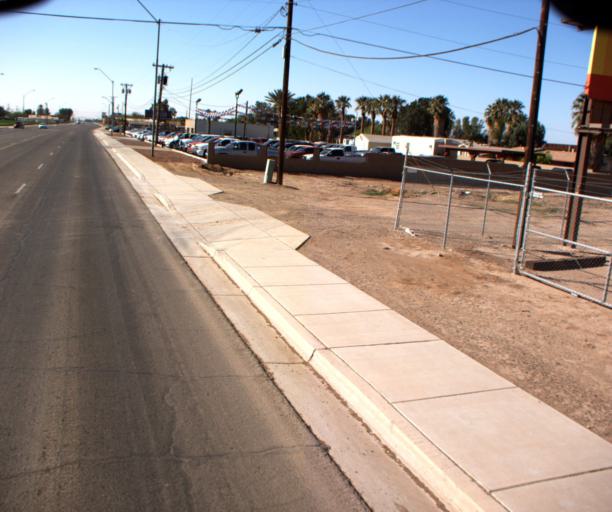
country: US
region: Arizona
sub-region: Yuma County
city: San Luis
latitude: 32.5602
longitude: -114.7848
